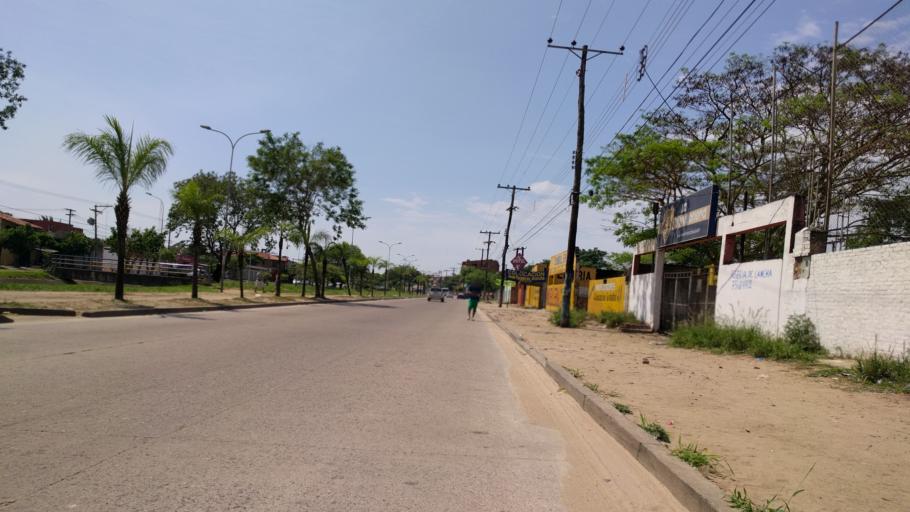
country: BO
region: Santa Cruz
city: Santa Cruz de la Sierra
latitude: -17.8147
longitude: -63.2055
